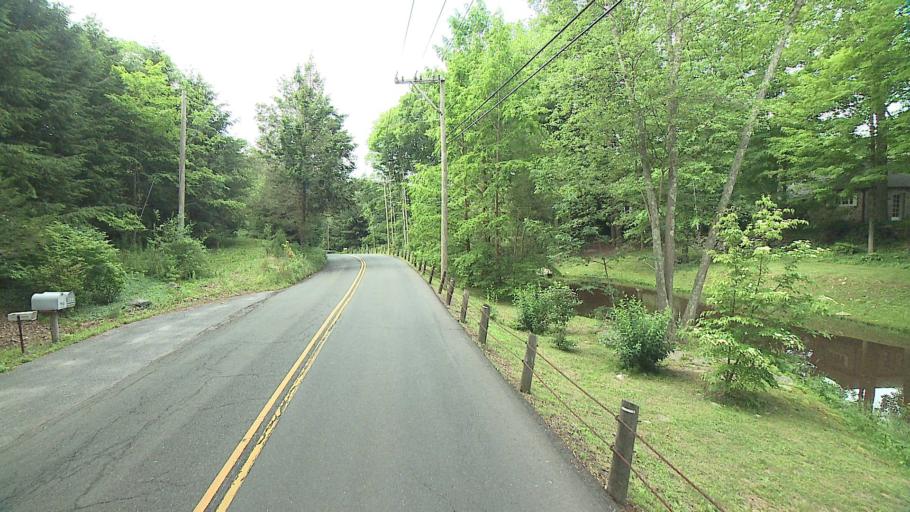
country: US
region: Connecticut
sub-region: New Haven County
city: Southbury
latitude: 41.4476
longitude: -73.1976
